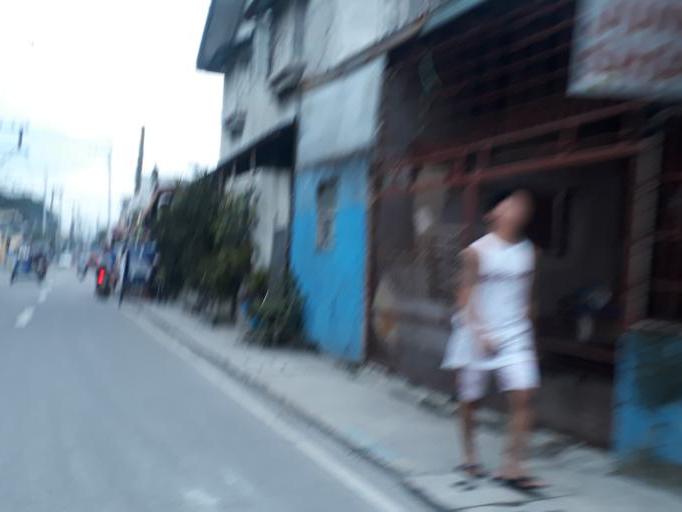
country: PH
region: Calabarzon
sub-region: Province of Rizal
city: Valenzuela
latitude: 14.6999
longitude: 120.9575
